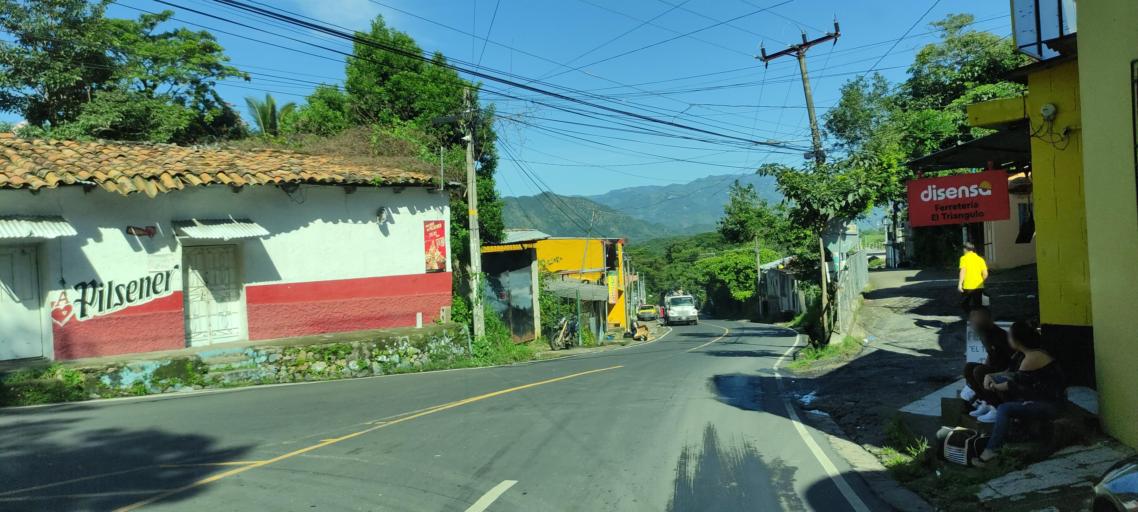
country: HN
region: Ocotepeque
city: Antigua Ocotepeque
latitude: 14.3181
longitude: -89.1715
